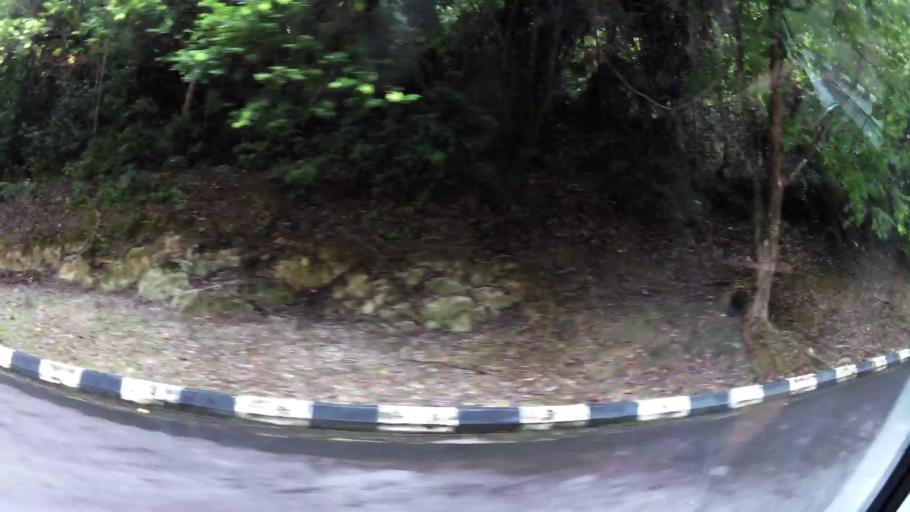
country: BN
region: Brunei and Muara
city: Bandar Seri Begawan
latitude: 4.8846
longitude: 114.9328
